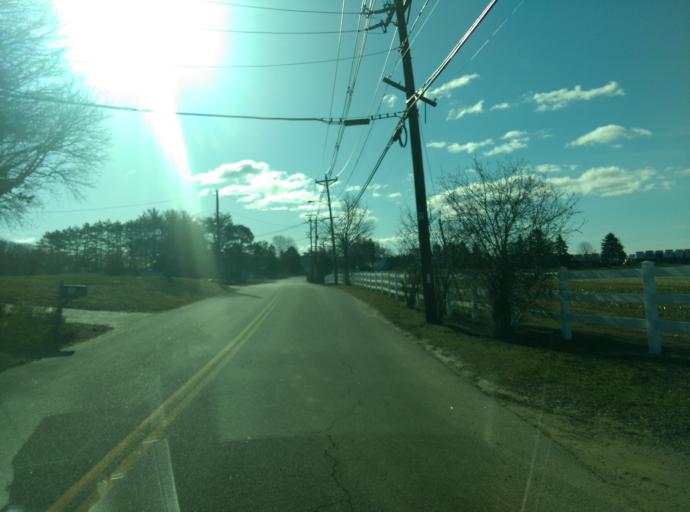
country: US
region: Massachusetts
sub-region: Essex County
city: Haverhill
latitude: 42.7551
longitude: -71.1199
